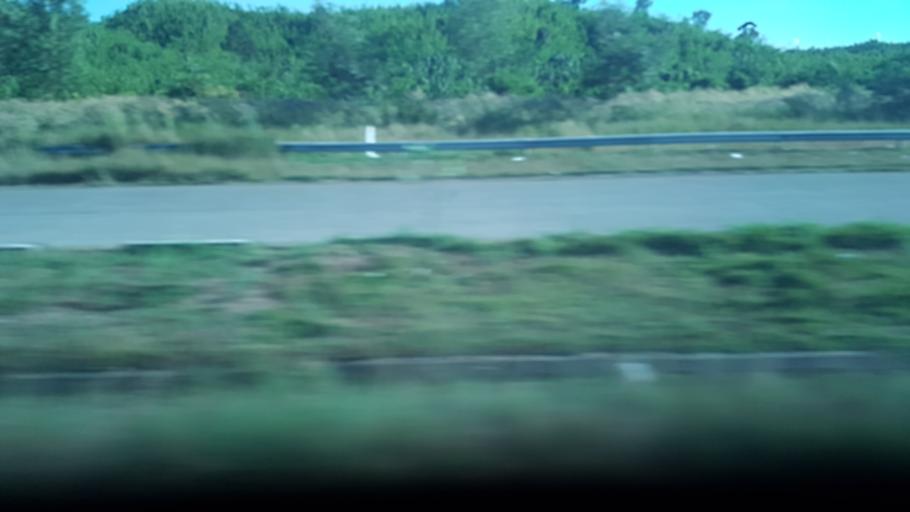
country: MM
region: Bago
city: Nyaunglebin
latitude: 17.6999
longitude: 96.4848
